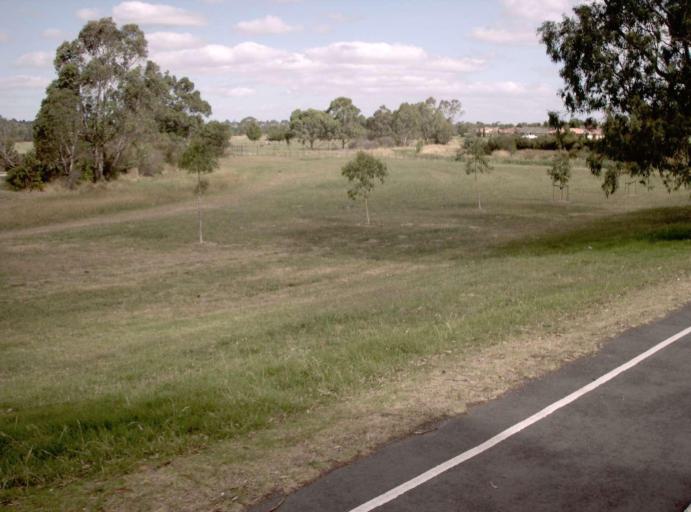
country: AU
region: Victoria
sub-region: Greater Dandenong
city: Dandenong North
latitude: -37.9661
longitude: 145.2244
